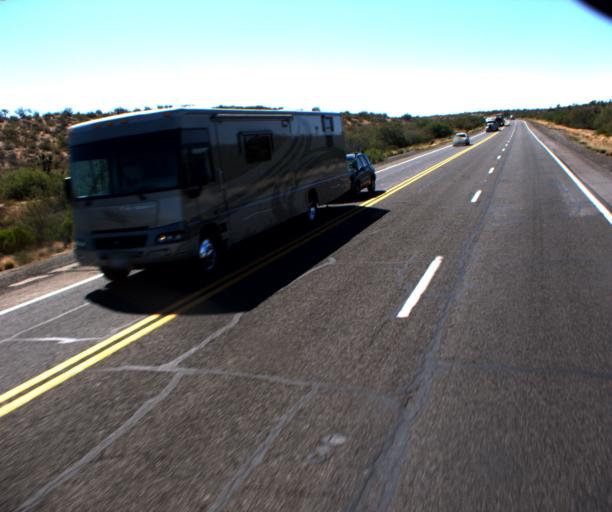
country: US
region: Arizona
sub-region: Yavapai County
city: Congress
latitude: 34.2018
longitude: -113.0623
